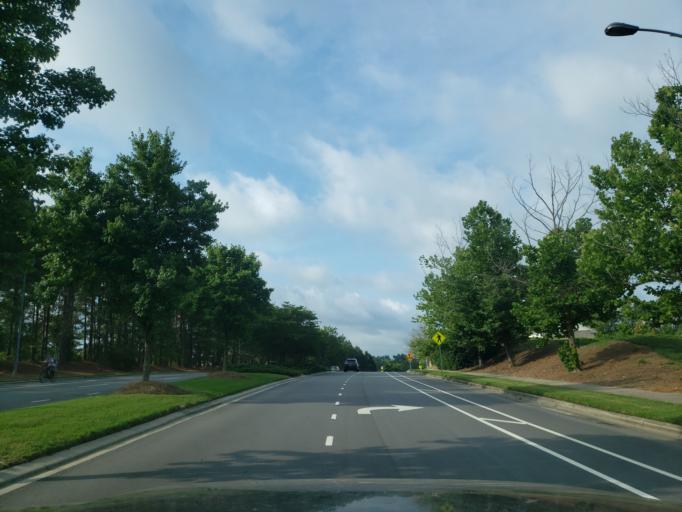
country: US
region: North Carolina
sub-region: Durham County
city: Durham
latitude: 35.9420
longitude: -78.9284
